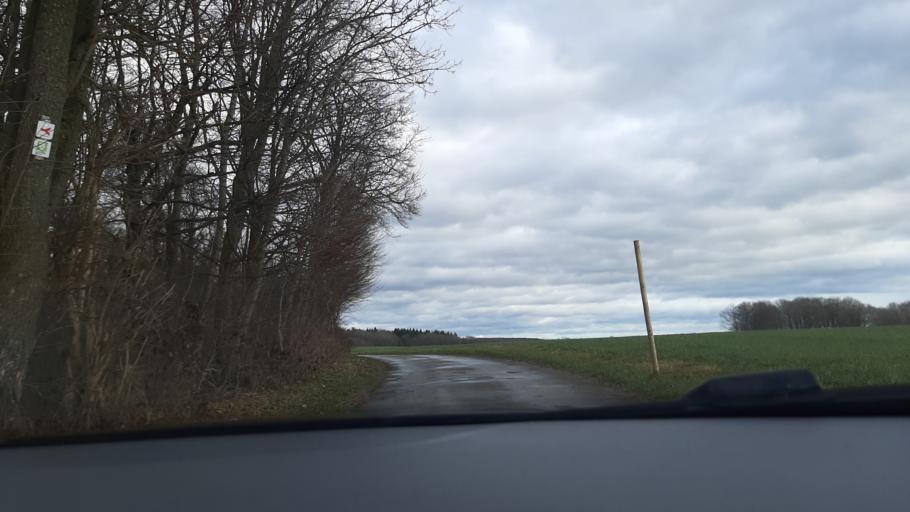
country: DE
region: Baden-Wuerttemberg
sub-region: Regierungsbezirk Stuttgart
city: Geislingen an der Steige
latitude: 48.6067
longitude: 9.8218
